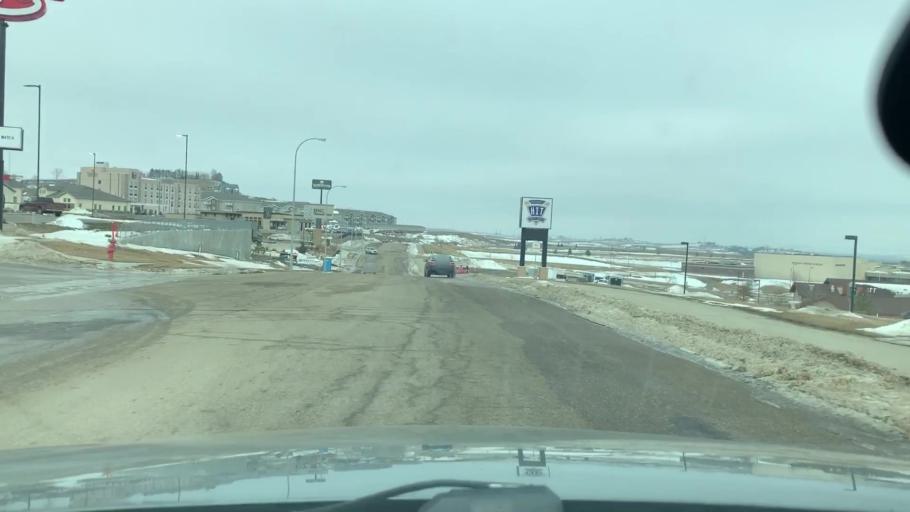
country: US
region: North Dakota
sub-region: Morton County
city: Mandan
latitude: 46.8483
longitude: -100.9086
